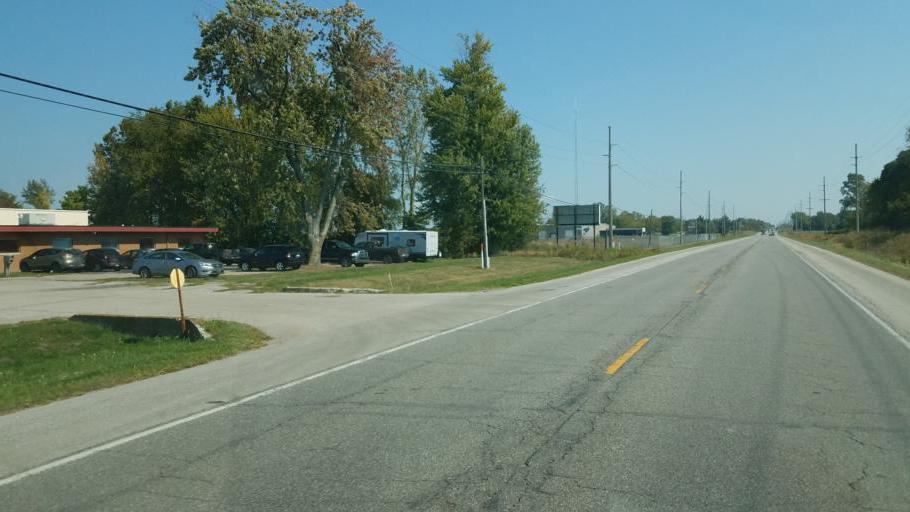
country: US
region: Indiana
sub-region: LaGrange County
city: Lagrange
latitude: 41.6416
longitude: -85.3926
